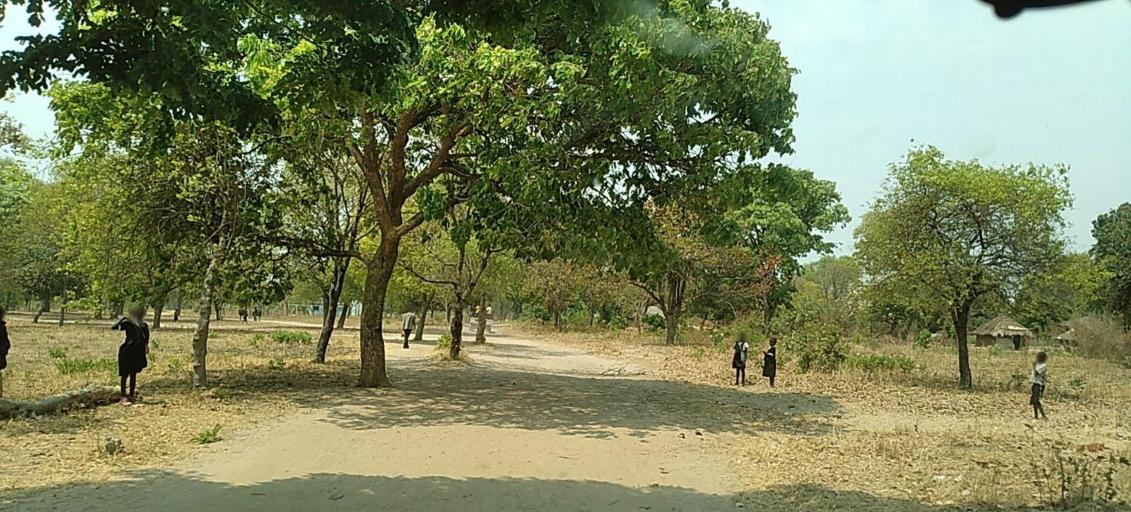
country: ZM
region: North-Western
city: Kabompo
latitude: -13.4975
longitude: 24.4661
